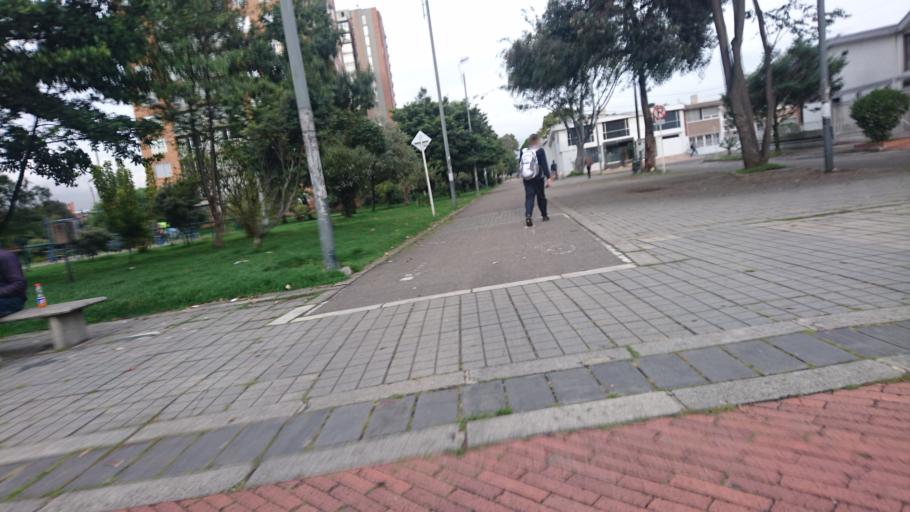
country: CO
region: Bogota D.C.
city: Barrio San Luis
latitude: 4.6789
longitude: -74.0618
